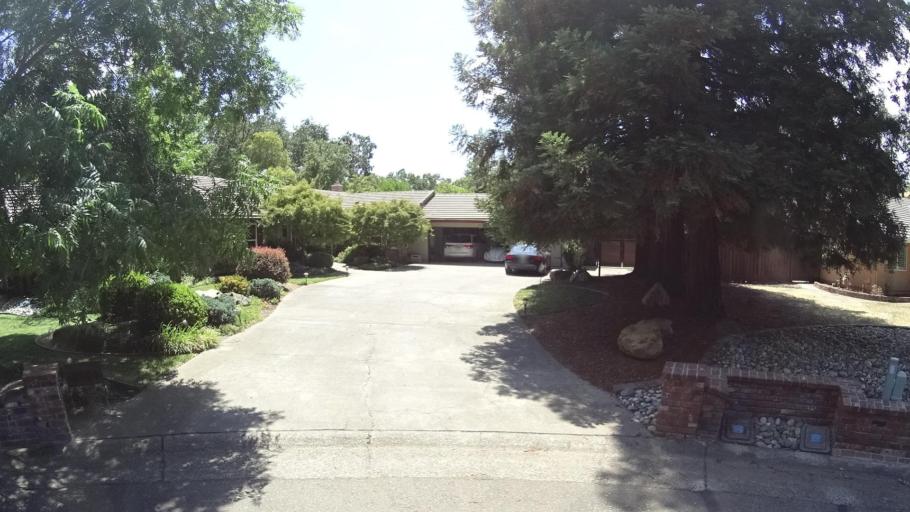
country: US
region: California
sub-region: Placer County
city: Rocklin
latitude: 38.8093
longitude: -121.2398
